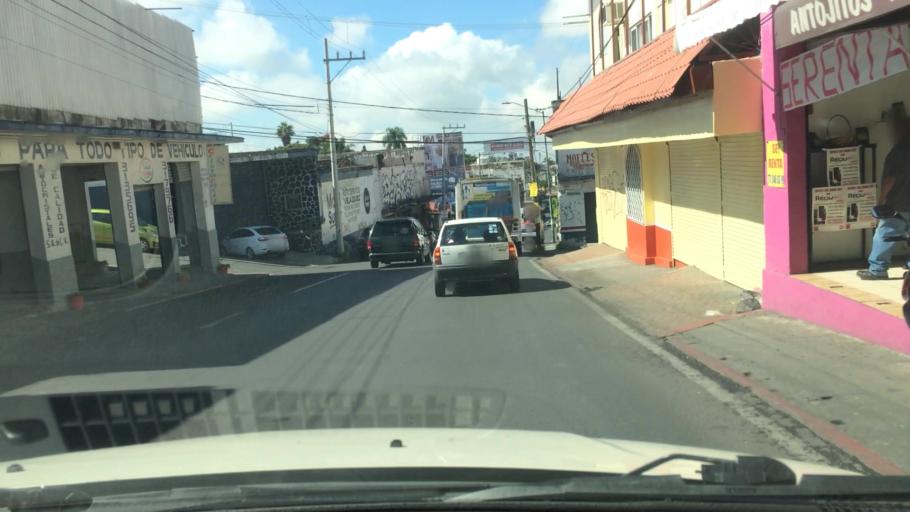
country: MX
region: Morelos
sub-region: Cuernavaca
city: Cuernavaca
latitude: 18.9363
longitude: -99.2406
